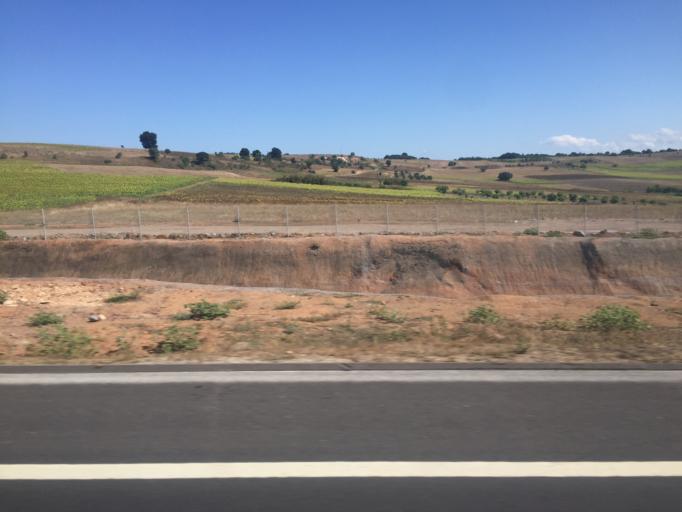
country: TR
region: Bursa
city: Mahmudiye
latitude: 40.2694
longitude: 28.6301
